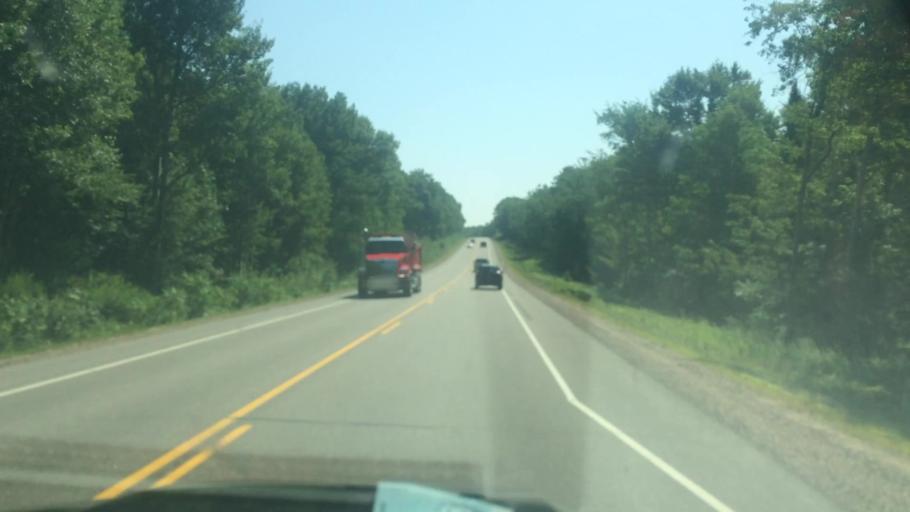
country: US
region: Wisconsin
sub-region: Oneida County
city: Rhinelander
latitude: 45.6174
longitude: -89.5179
